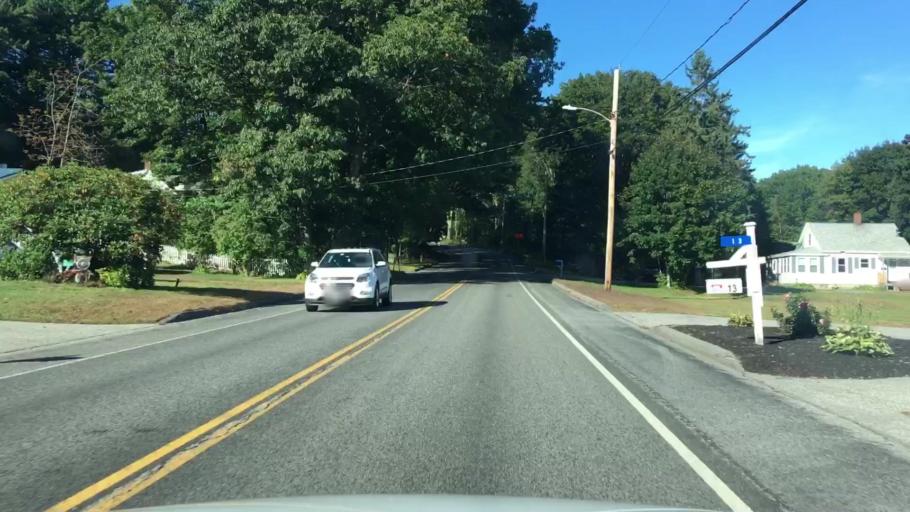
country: US
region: Maine
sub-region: Androscoggin County
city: Lisbon Falls
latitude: 44.0065
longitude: -70.0702
